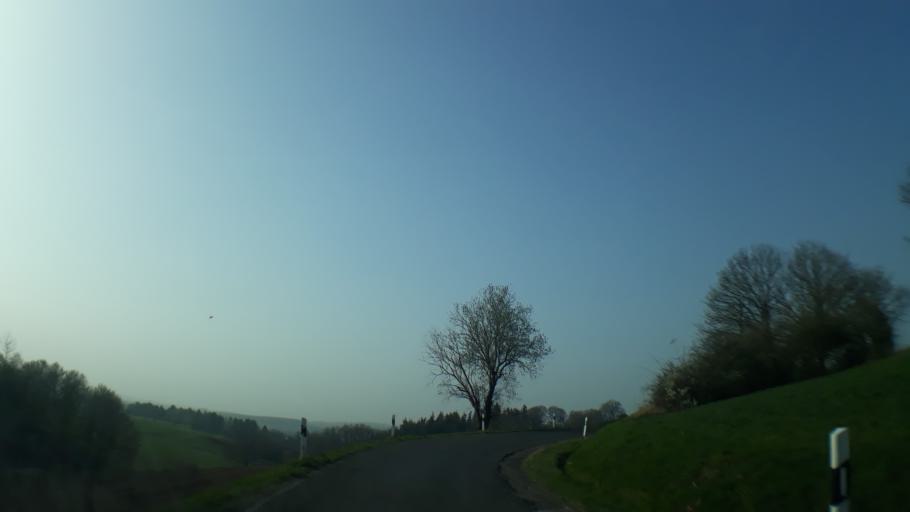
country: DE
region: North Rhine-Westphalia
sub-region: Regierungsbezirk Koln
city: Bad Munstereifel
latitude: 50.5392
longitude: 6.7317
